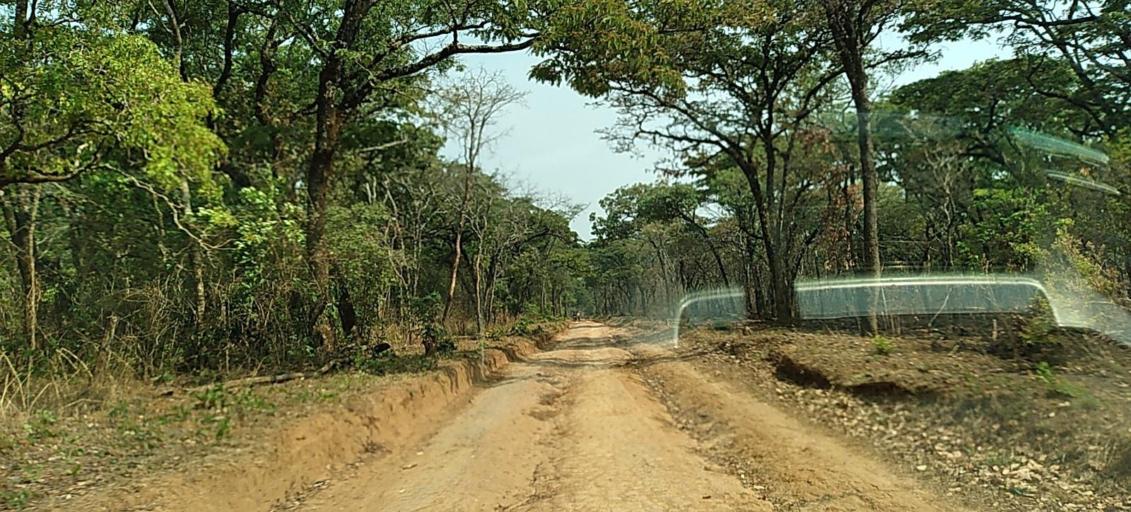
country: ZM
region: North-Western
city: Kansanshi
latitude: -12.0599
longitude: 26.8883
